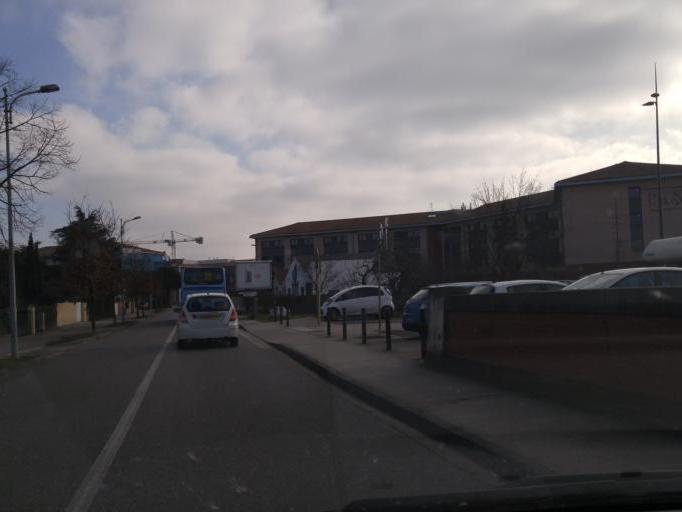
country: FR
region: Midi-Pyrenees
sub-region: Departement de la Haute-Garonne
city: Blagnac
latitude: 43.6405
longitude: 1.3757
